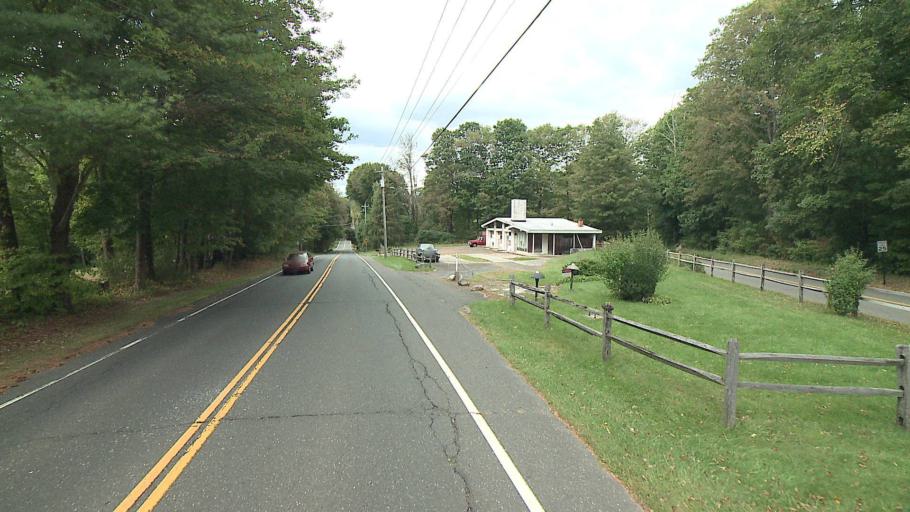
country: US
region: Connecticut
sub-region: Fairfield County
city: Ridgefield
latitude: 41.2482
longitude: -73.4869
